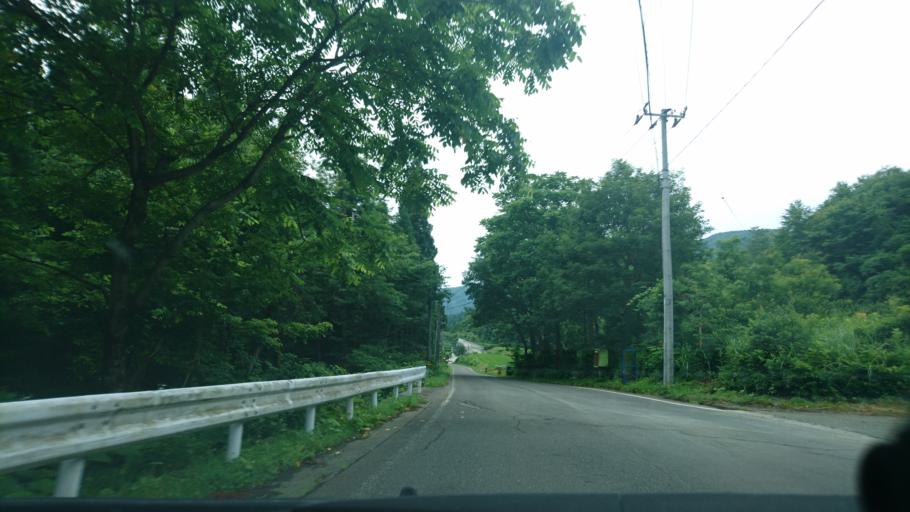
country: JP
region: Akita
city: Yokotemachi
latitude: 39.1734
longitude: 140.7319
